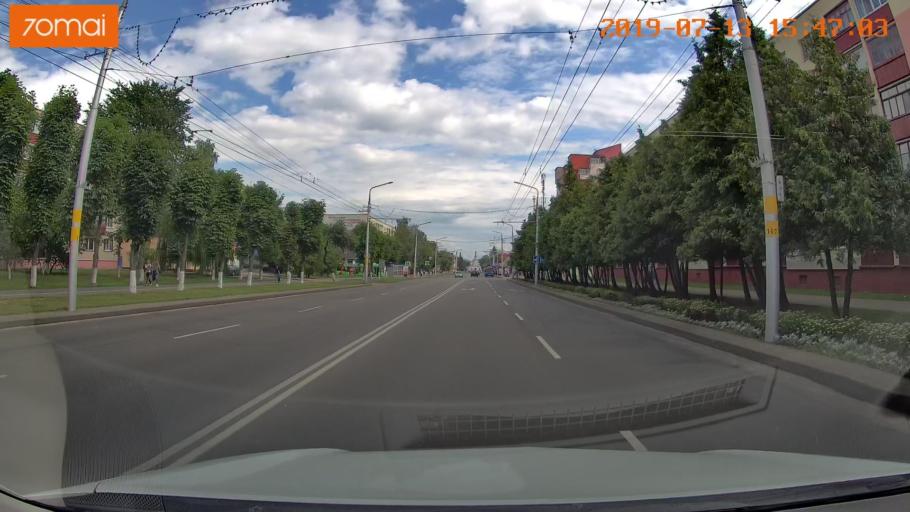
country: BY
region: Mogilev
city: Babruysk
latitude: 53.1497
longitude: 29.2282
